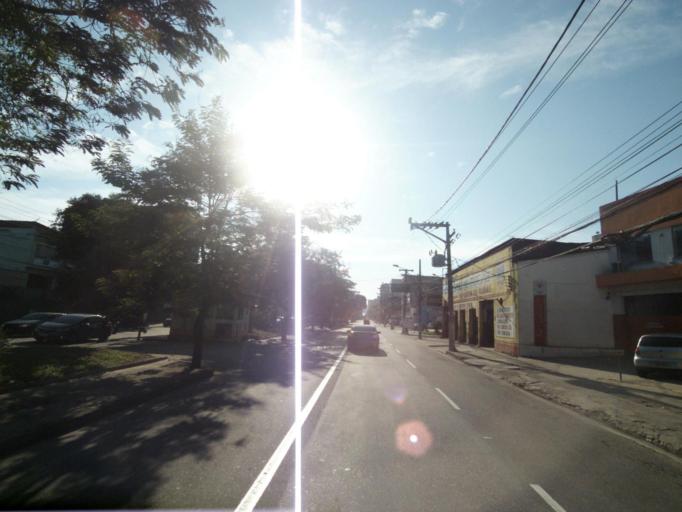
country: BR
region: Rio de Janeiro
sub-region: Niteroi
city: Niteroi
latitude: -22.8807
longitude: -43.1063
